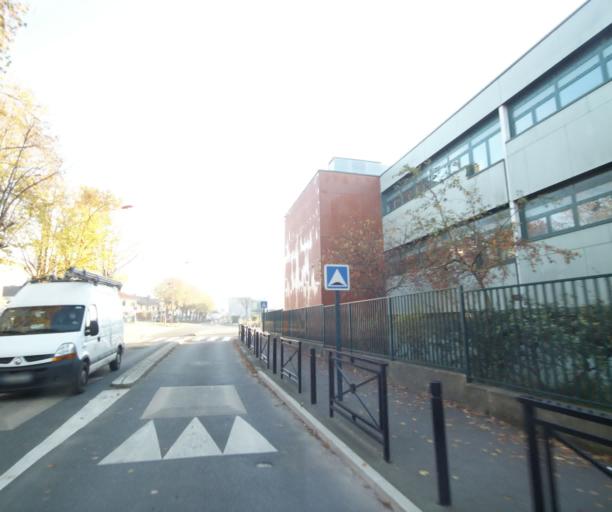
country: FR
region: Ile-de-France
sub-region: Departement du Val-d'Oise
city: Gonesse
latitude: 48.9874
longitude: 2.4420
